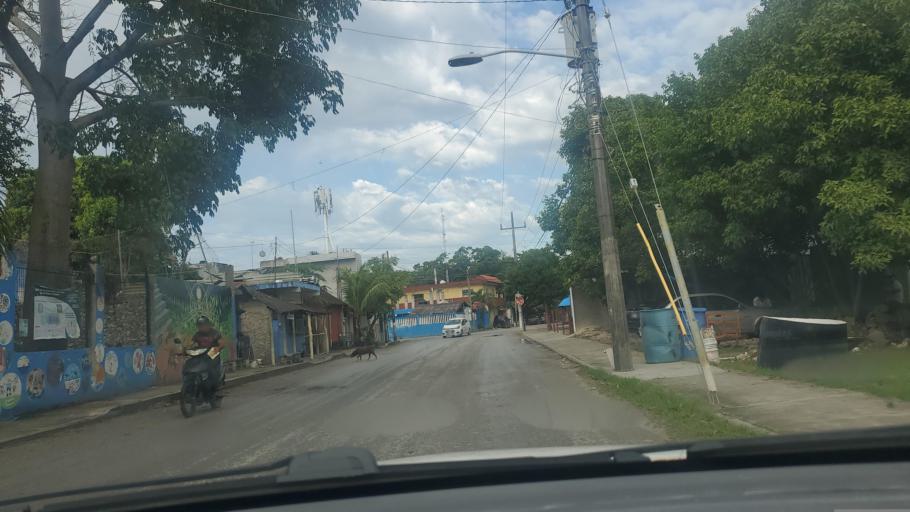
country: MX
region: Quintana Roo
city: Tulum
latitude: 20.2110
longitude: -87.4690
